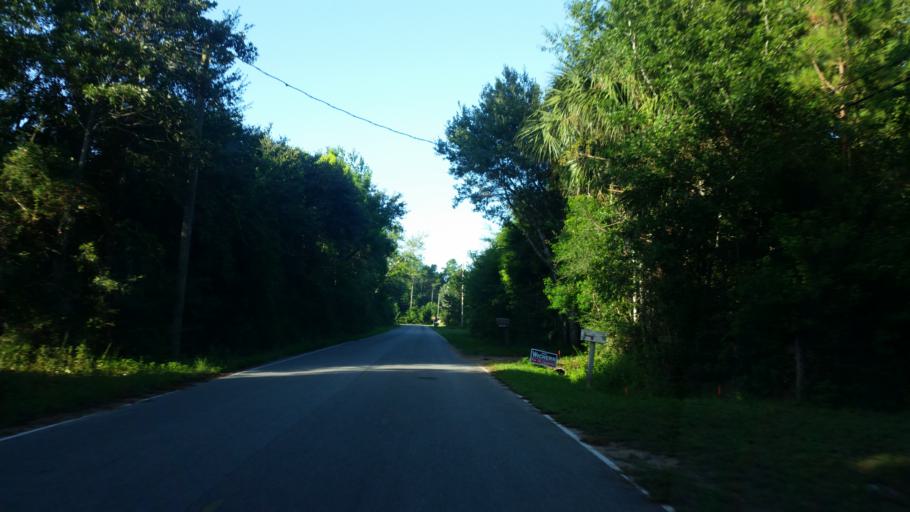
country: US
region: Florida
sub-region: Escambia County
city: Myrtle Grove
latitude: 30.4086
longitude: -87.3238
